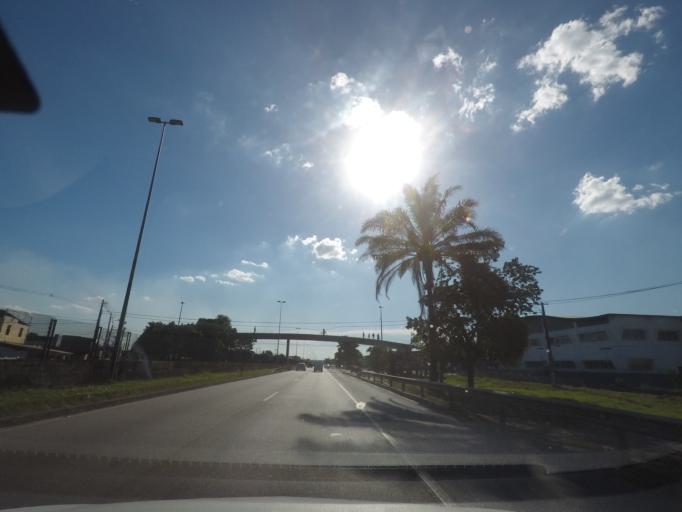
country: BR
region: Rio de Janeiro
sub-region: Petropolis
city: Petropolis
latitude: -22.6486
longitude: -43.2303
